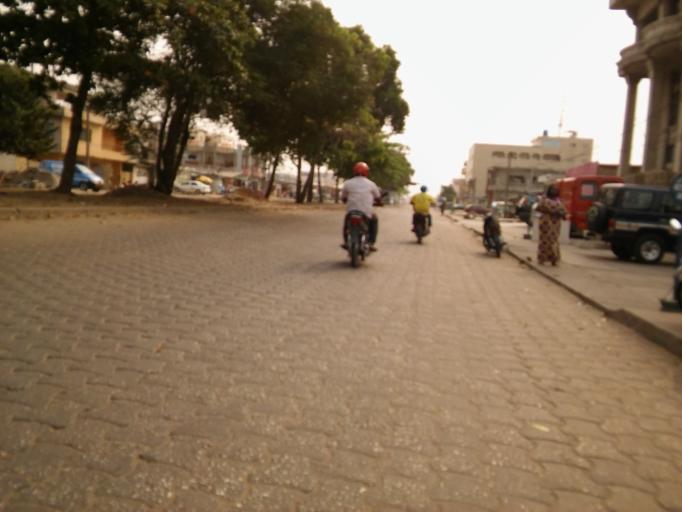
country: BJ
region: Littoral
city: Cotonou
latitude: 6.3785
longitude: 2.4086
